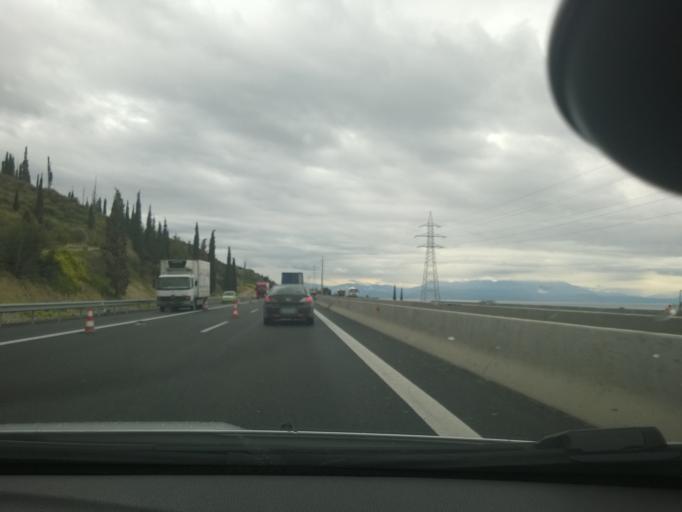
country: GR
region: Peloponnese
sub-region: Nomos Korinthias
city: Xylokastro
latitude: 38.1177
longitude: 22.5144
